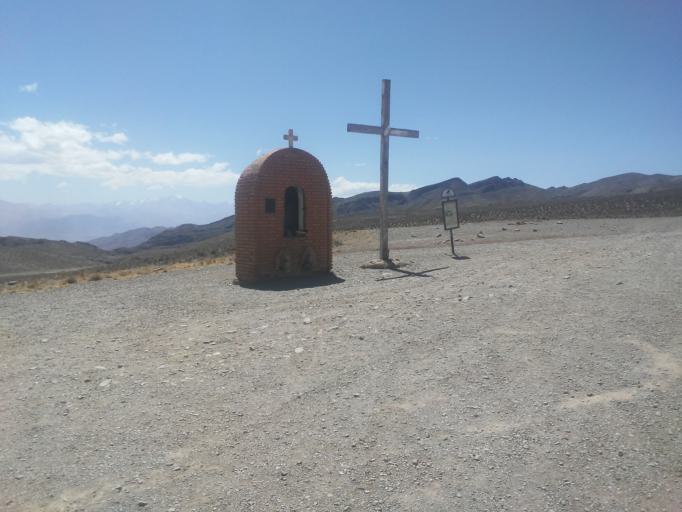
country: AR
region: Mendoza
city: Las Heras
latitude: -32.4857
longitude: -69.1159
